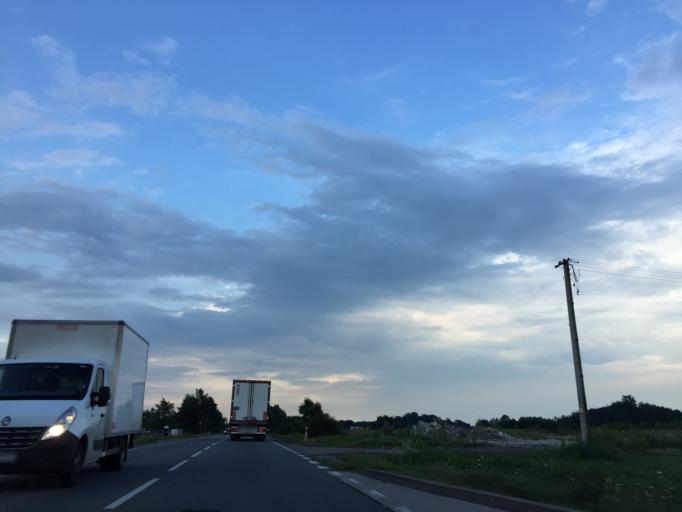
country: PL
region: Masovian Voivodeship
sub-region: Powiat minski
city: Minsk Mazowiecki
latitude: 52.2133
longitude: 21.5380
